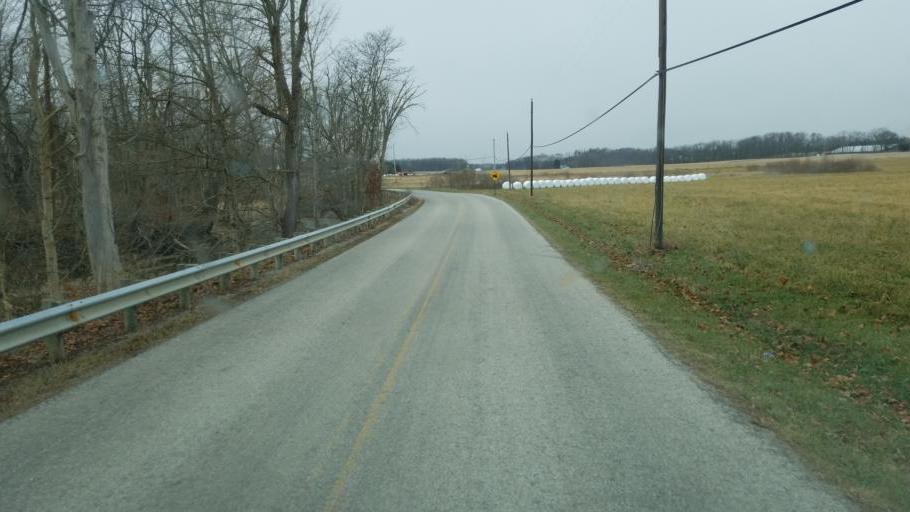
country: US
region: Ohio
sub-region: Richland County
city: Lexington
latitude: 40.6185
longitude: -82.5791
